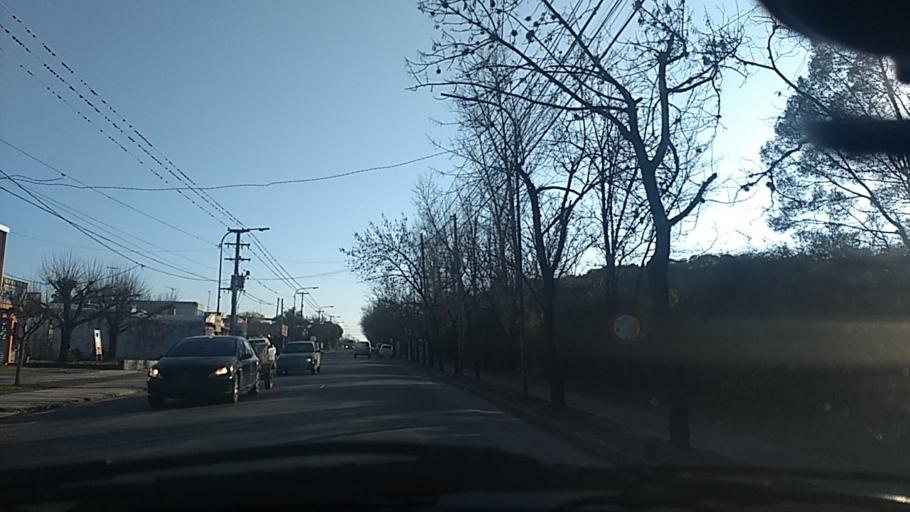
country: AR
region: Cordoba
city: Salsipuedes
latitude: -31.1354
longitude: -64.2960
